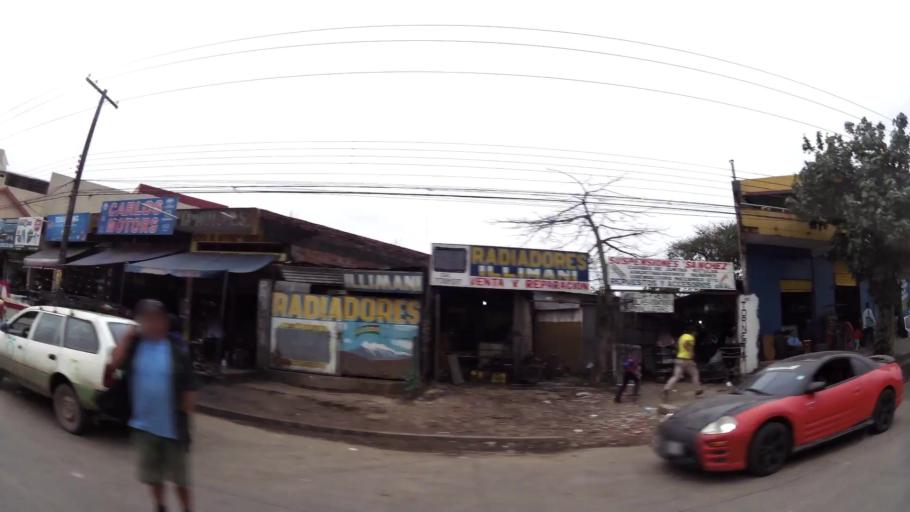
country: BO
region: Santa Cruz
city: Santa Cruz de la Sierra
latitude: -17.8095
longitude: -63.1933
